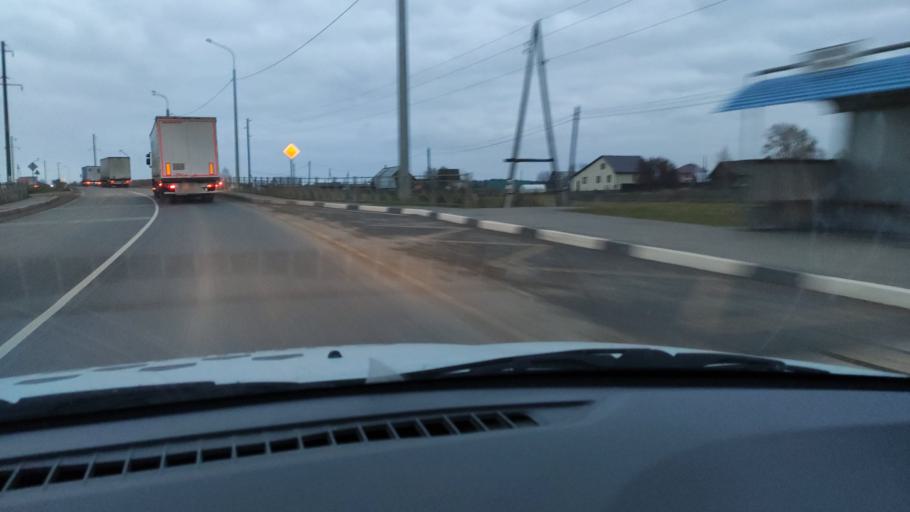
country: RU
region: Kirov
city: Kostino
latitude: 58.8521
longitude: 53.2642
